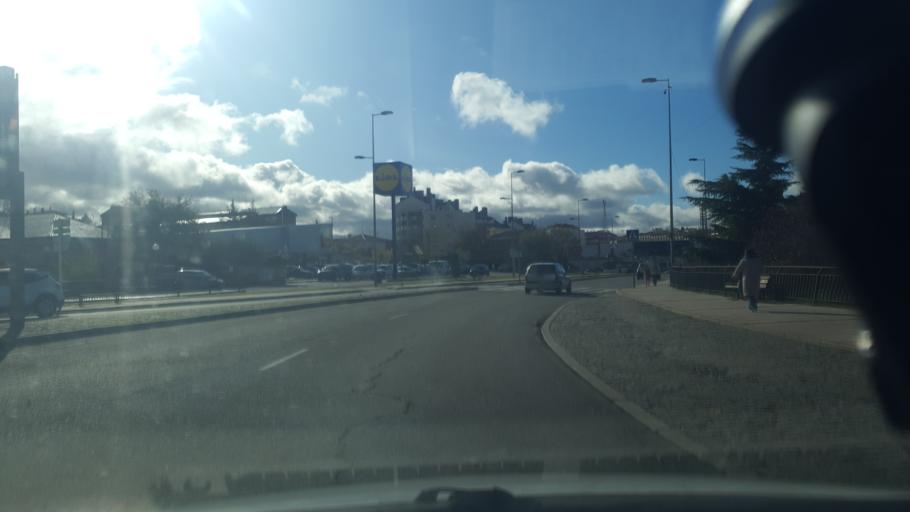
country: ES
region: Castille and Leon
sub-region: Provincia de Avila
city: Avila
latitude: 40.6598
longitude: -4.6799
